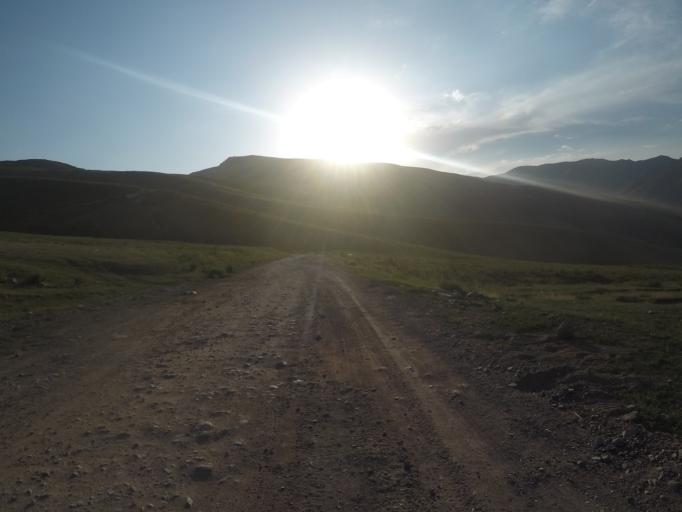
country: KG
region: Chuy
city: Bishkek
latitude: 42.6533
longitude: 74.6560
